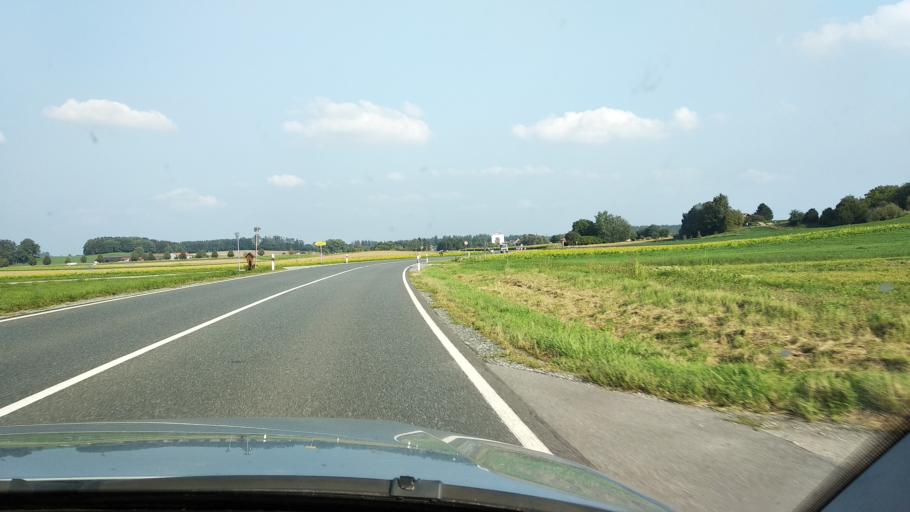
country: DE
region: Bavaria
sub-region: Upper Bavaria
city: Steinhoring
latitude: 48.0848
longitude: 12.0715
